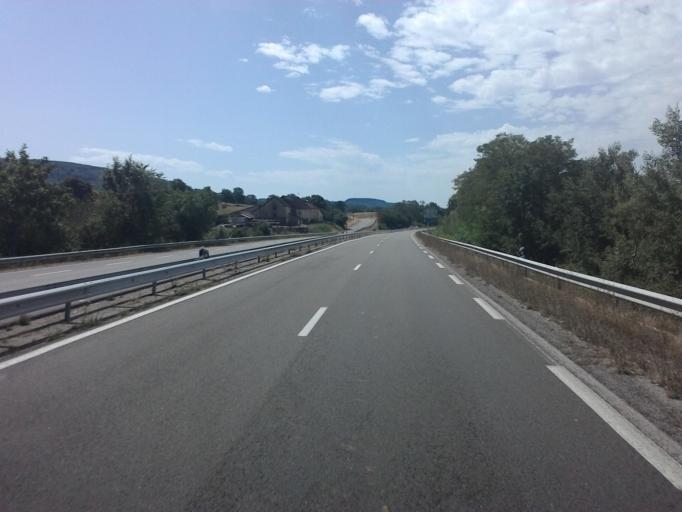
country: FR
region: Bourgogne
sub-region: Departement de Saone-et-Loire
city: Cuiseaux
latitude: 46.5069
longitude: 5.3872
